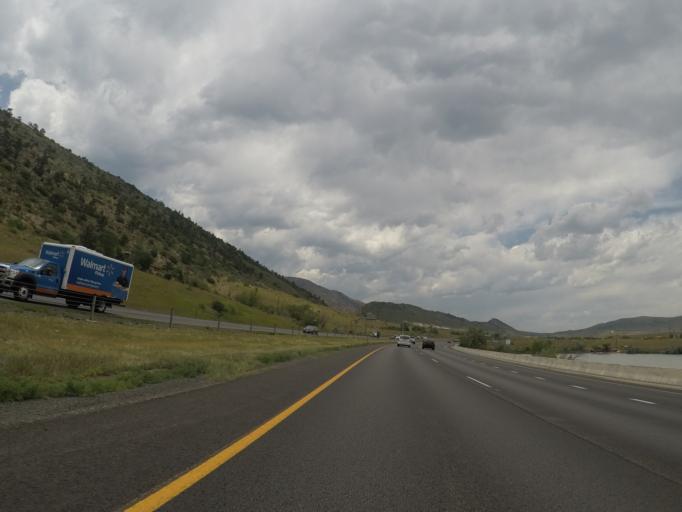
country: US
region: Colorado
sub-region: Jefferson County
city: Indian Hills
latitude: 39.6453
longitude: -105.1789
